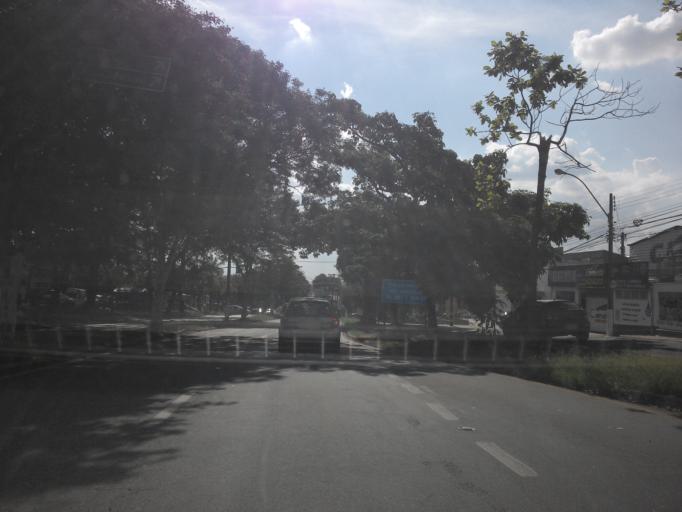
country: BR
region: Sao Paulo
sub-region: Campinas
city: Campinas
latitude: -22.9357
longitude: -47.0369
